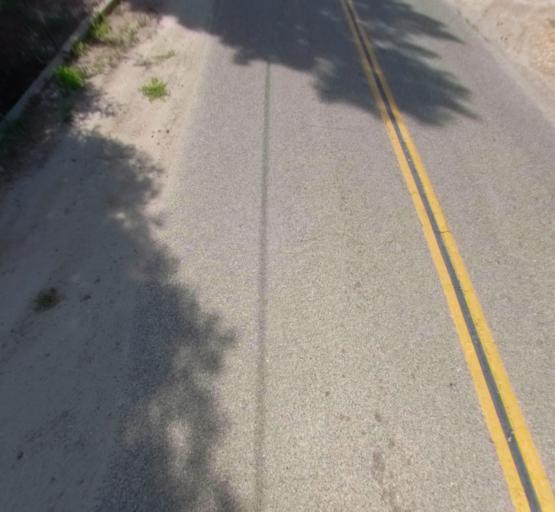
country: US
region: California
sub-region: Madera County
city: Chowchilla
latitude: 37.0918
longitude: -120.2870
